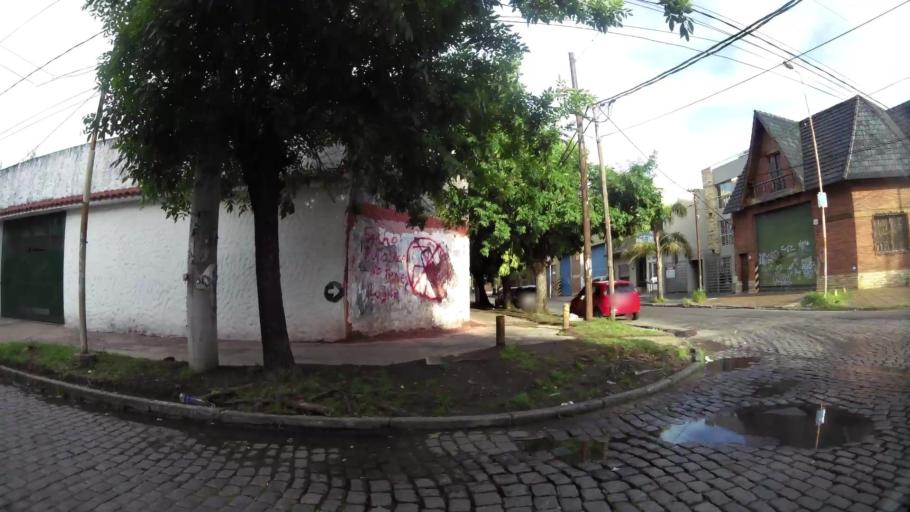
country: AR
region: Buenos Aires
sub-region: Partido de Moron
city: Moron
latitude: -34.6570
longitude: -58.6186
